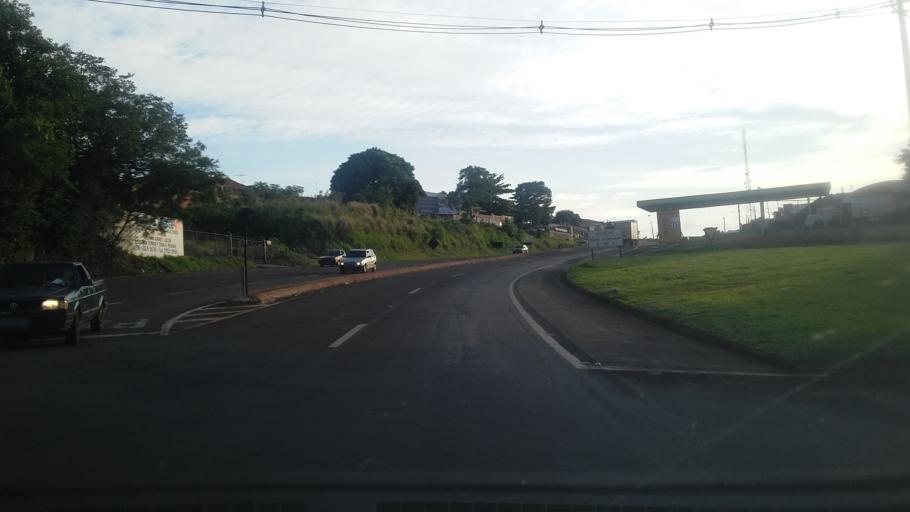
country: BR
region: Parana
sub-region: Assai
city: Assai
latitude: -23.1904
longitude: -50.6470
